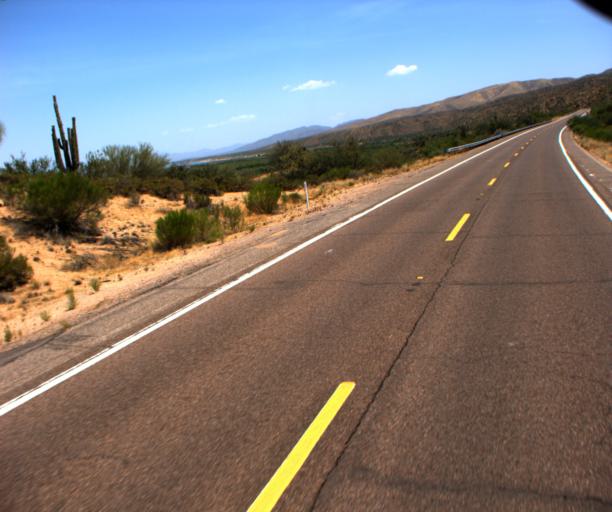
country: US
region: Arizona
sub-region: Gila County
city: Tonto Basin
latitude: 33.7734
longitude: -111.2607
